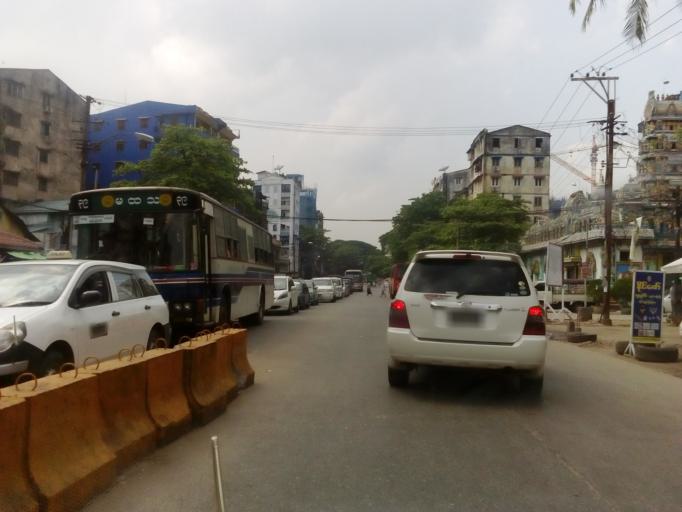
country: MM
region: Yangon
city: Yangon
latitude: 16.7917
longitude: 96.1726
